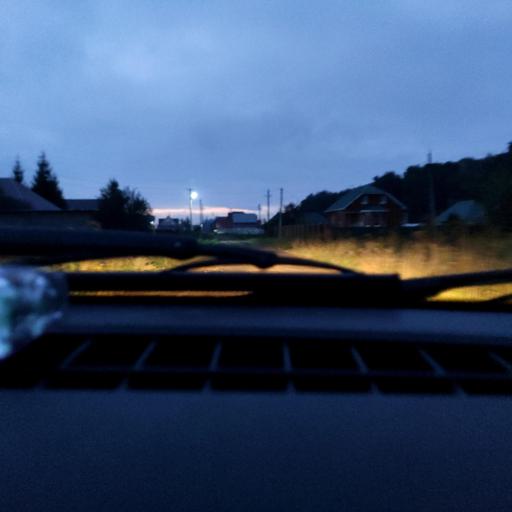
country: RU
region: Bashkortostan
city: Iglino
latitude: 54.7316
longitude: 56.3276
